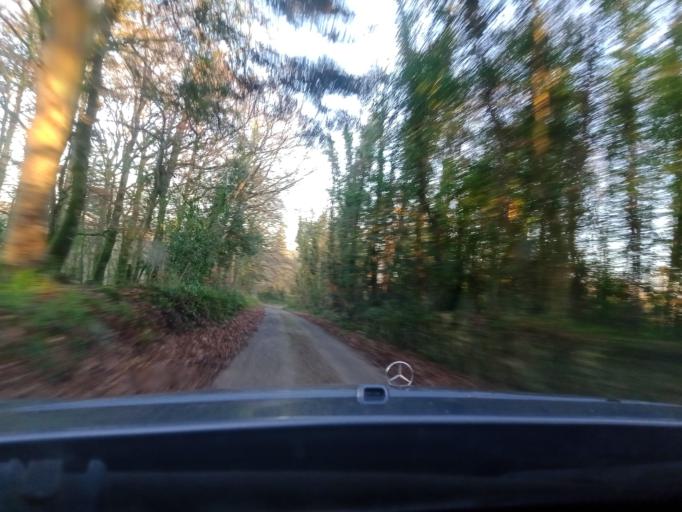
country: IE
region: Leinster
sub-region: Kilkenny
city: Graiguenamanagh
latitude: 52.4690
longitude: -6.9446
